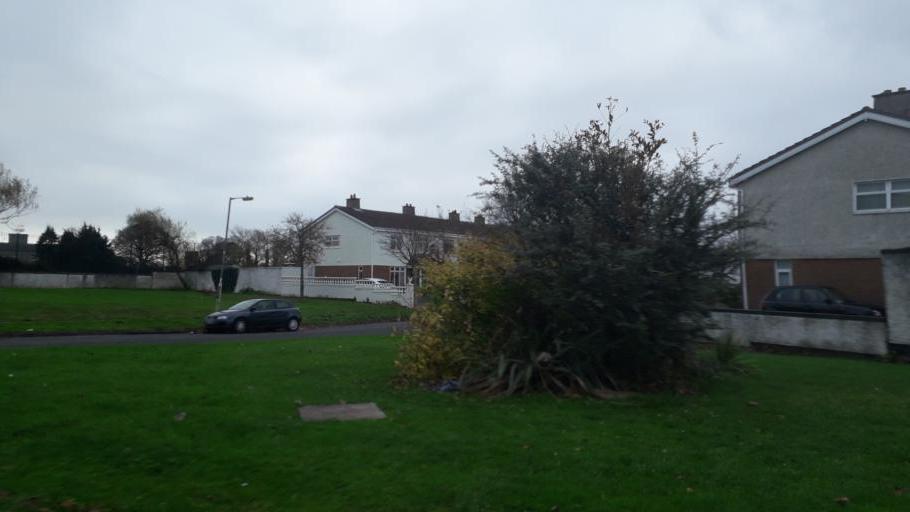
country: IE
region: Leinster
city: Glasnevin
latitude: 53.3817
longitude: -6.2752
